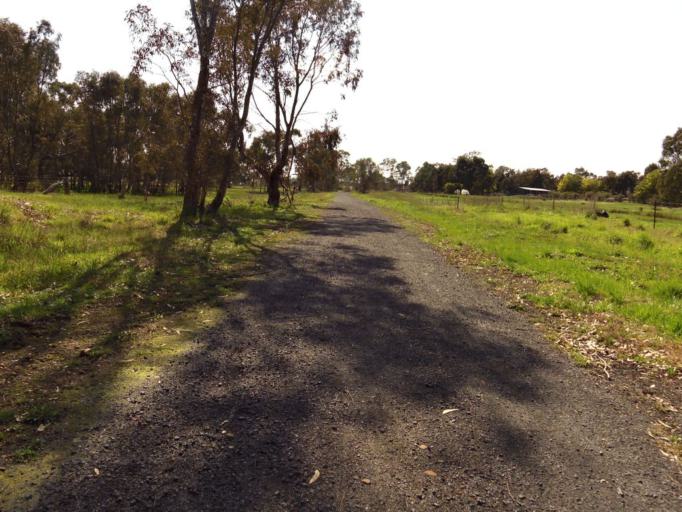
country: AU
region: Victoria
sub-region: Murrindindi
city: Alexandra
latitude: -37.1046
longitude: 145.6167
